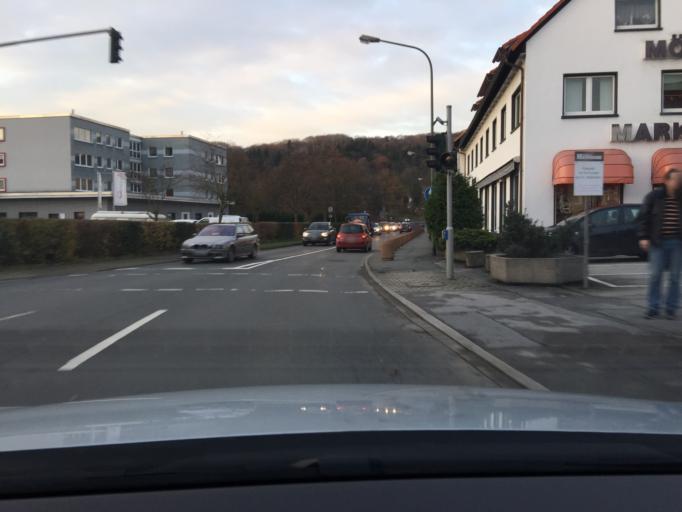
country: DE
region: North Rhine-Westphalia
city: Hattingen
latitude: 51.3731
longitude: 7.1364
